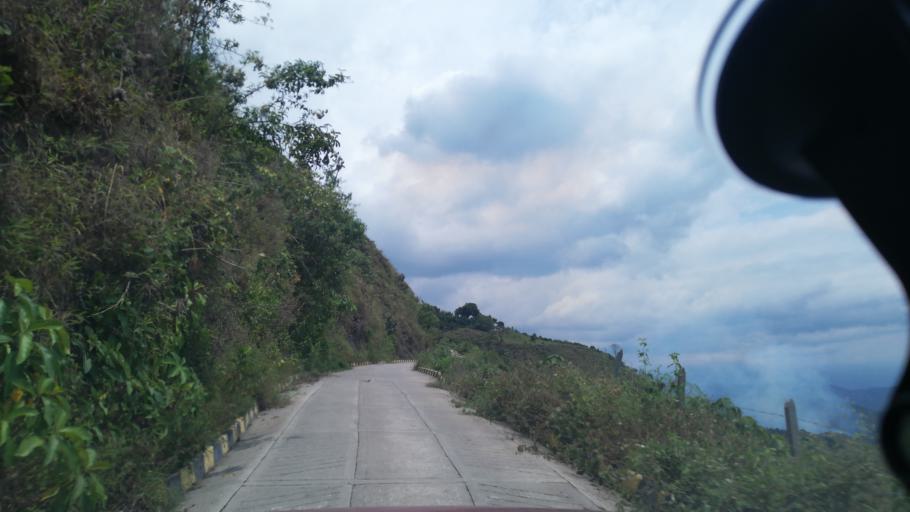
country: CO
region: Cundinamarca
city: Vergara
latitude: 5.1975
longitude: -74.2754
